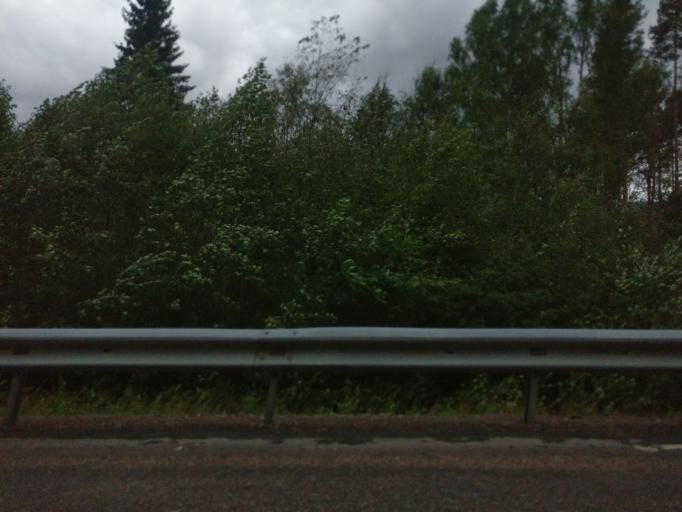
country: SE
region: Vaermland
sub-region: Torsby Kommun
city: Torsby
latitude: 60.5965
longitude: 13.0710
